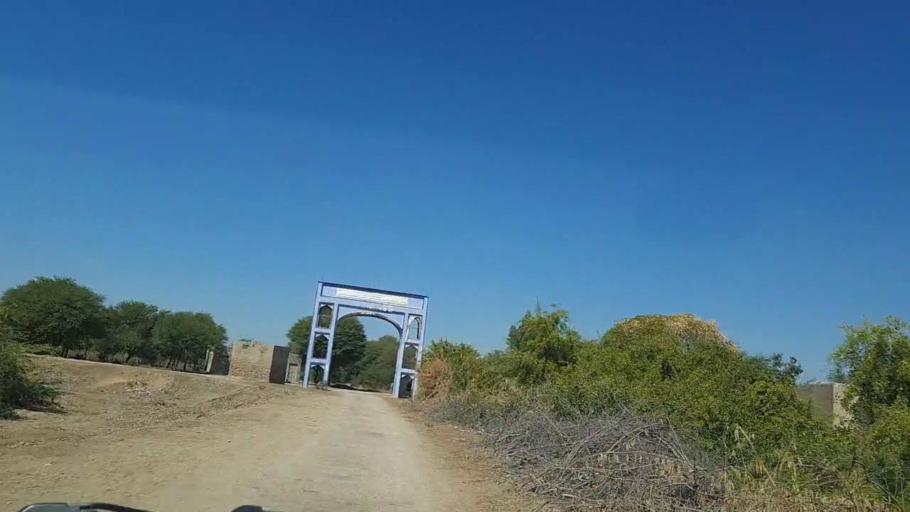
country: PK
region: Sindh
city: Dhoro Naro
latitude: 25.5344
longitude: 69.5008
